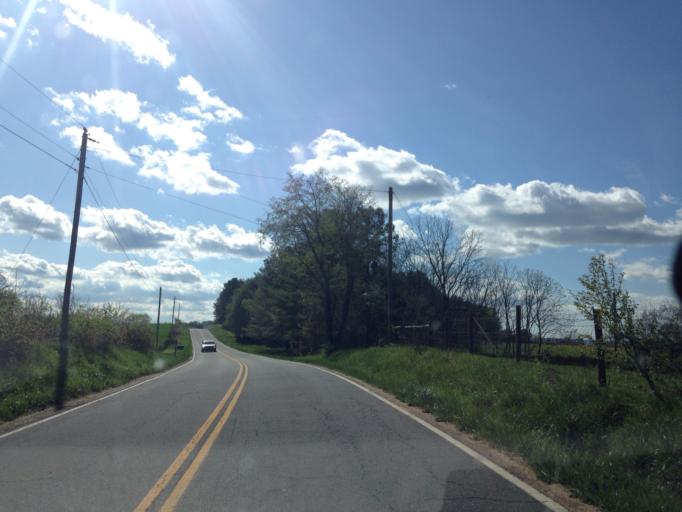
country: US
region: Maryland
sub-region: Frederick County
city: Point of Rocks
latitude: 39.2855
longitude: -77.5706
